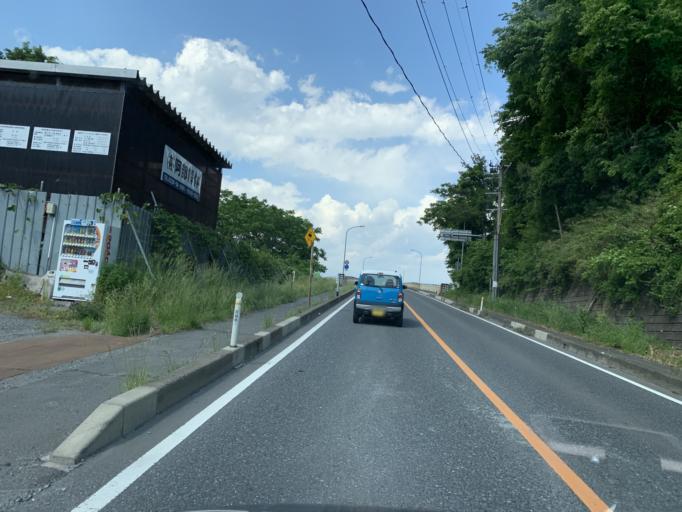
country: JP
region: Miyagi
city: Wakuya
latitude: 38.4961
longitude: 141.1156
